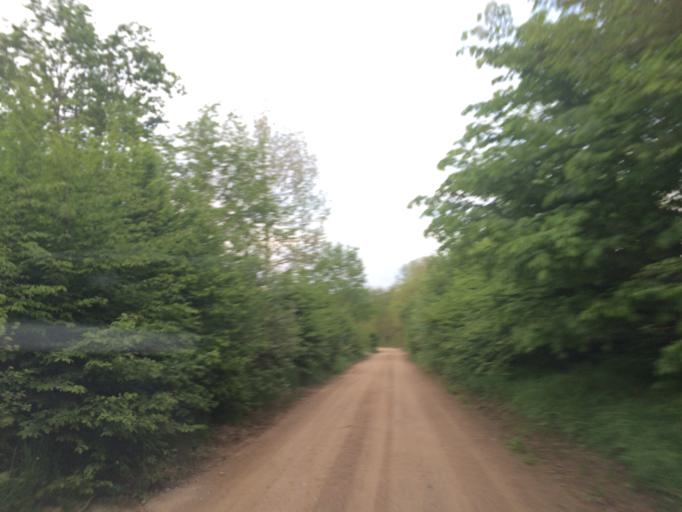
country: PL
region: Warmian-Masurian Voivodeship
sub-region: Powiat nowomiejski
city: Kurzetnik
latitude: 53.3388
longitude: 19.4986
